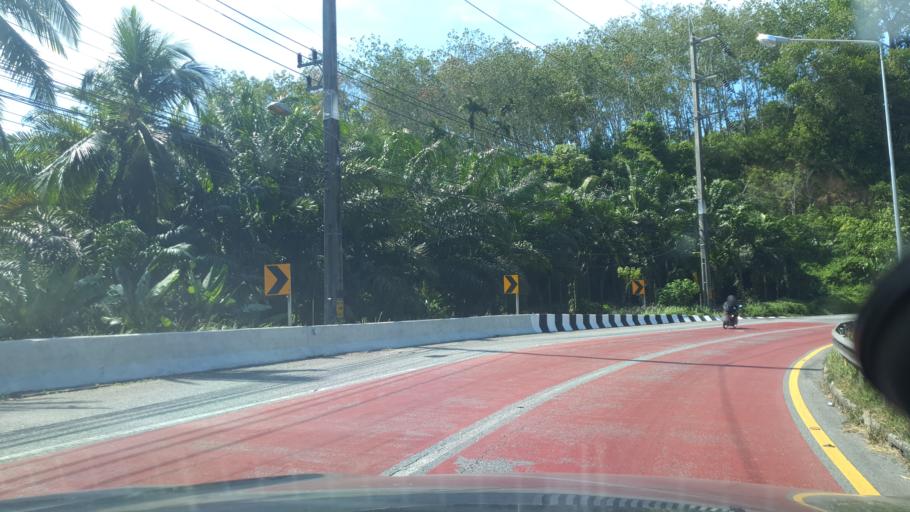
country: TH
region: Phangnga
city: Takua Thung
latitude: 8.2772
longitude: 98.3606
